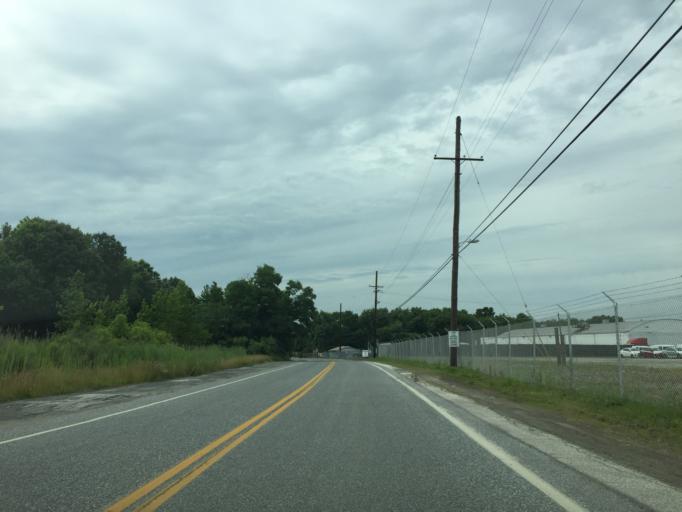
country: US
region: Maryland
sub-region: Baltimore County
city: Edgemere
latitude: 39.2748
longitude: -76.4626
